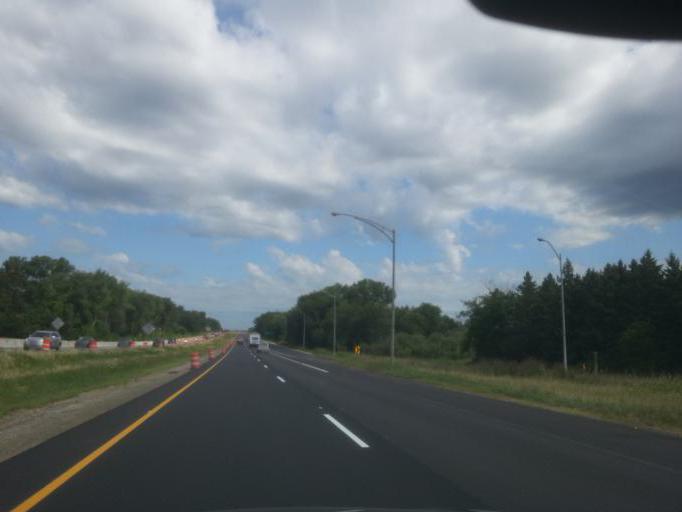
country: US
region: Wisconsin
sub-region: Dane County
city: Monona
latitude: 43.0859
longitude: -89.3118
